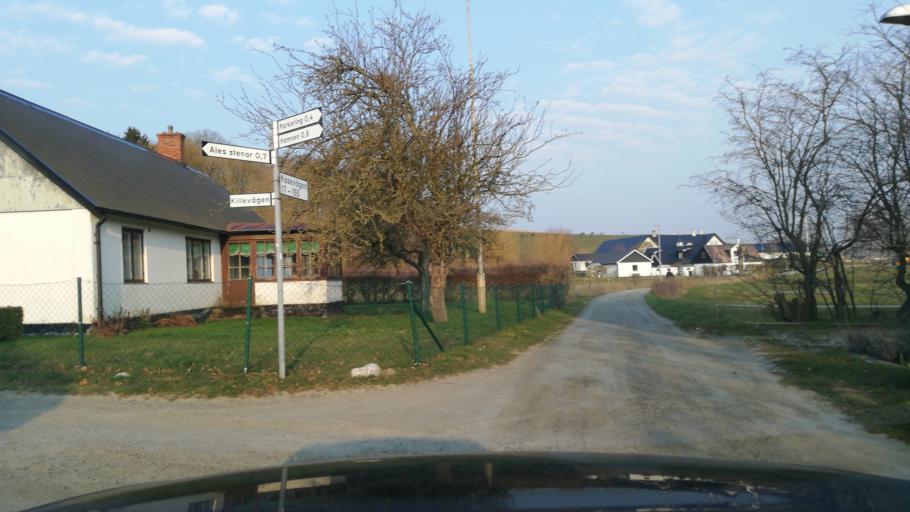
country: SE
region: Skane
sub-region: Ystads Kommun
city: Kopingebro
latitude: 55.3857
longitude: 14.0628
